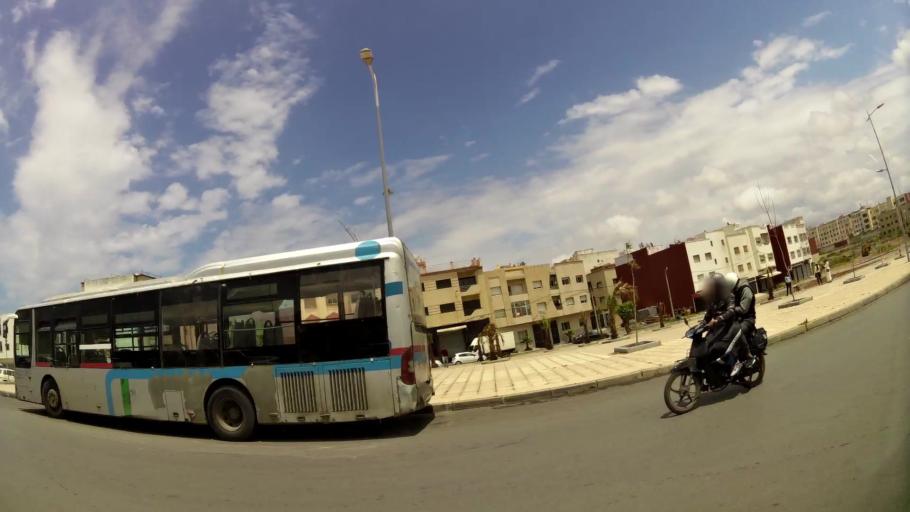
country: MA
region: Rabat-Sale-Zemmour-Zaer
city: Sale
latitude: 34.0439
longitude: -6.8244
